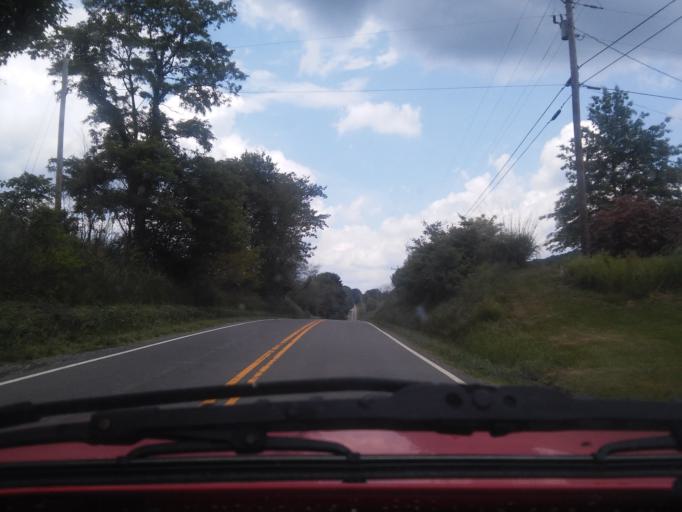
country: US
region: Virginia
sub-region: Craig County
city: New Castle
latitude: 37.4233
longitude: -80.2563
